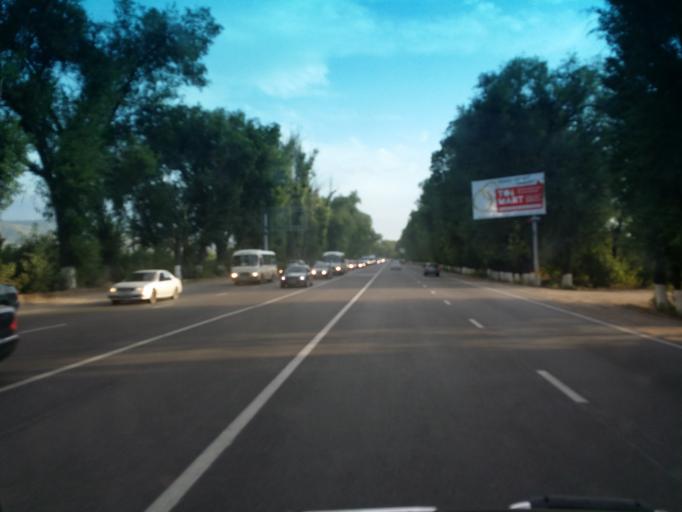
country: KZ
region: Almaty Oblysy
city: Pervomayskiy
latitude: 43.3125
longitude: 77.0192
